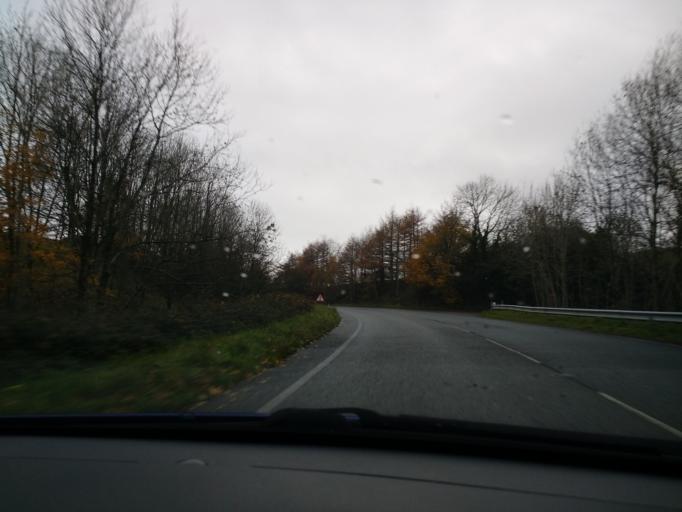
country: GB
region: England
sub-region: Cumbria
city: Millom
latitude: 54.2720
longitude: -3.2483
